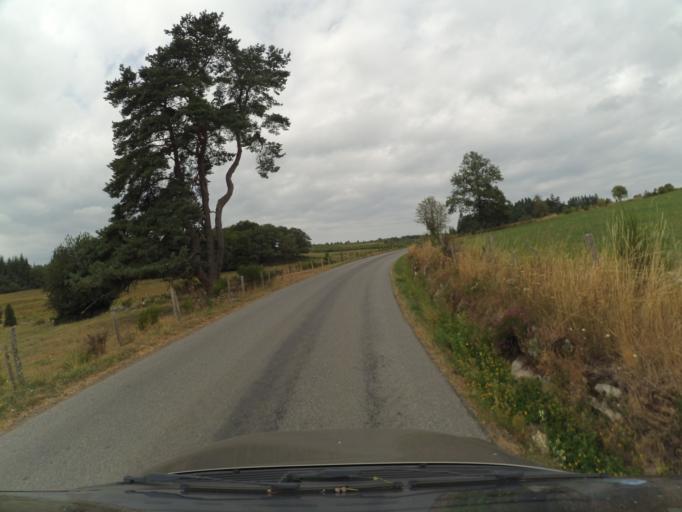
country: FR
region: Limousin
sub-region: Departement de la Correze
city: Meymac
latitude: 45.6553
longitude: 2.0985
